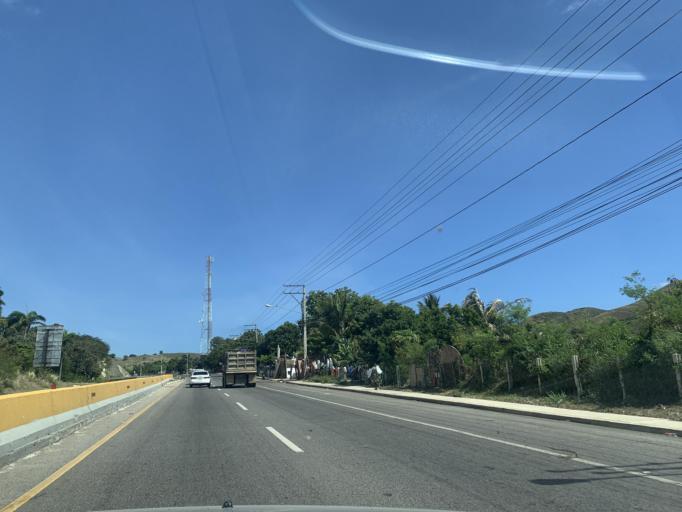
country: DO
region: Puerto Plata
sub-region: Puerto Plata
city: Puerto Plata
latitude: 19.8256
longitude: -70.7466
